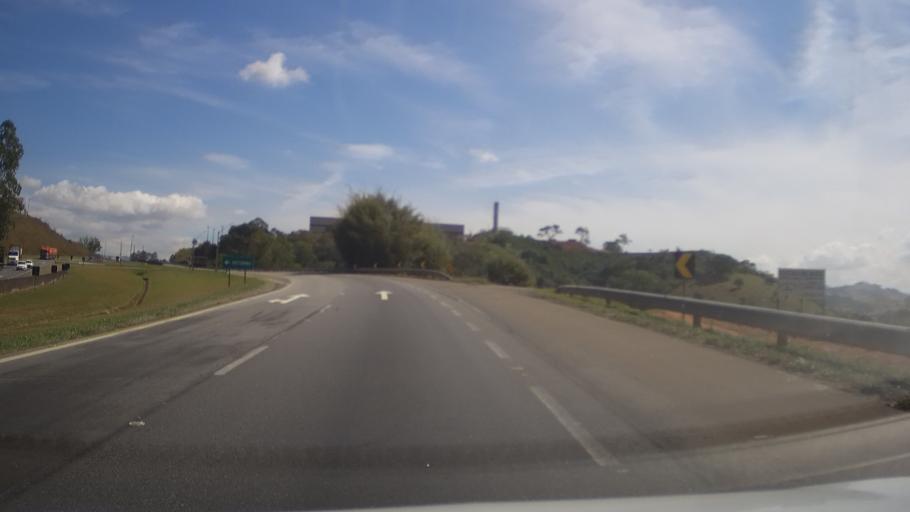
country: BR
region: Minas Gerais
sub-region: Cambui
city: Cambui
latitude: -22.5677
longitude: -46.0410
